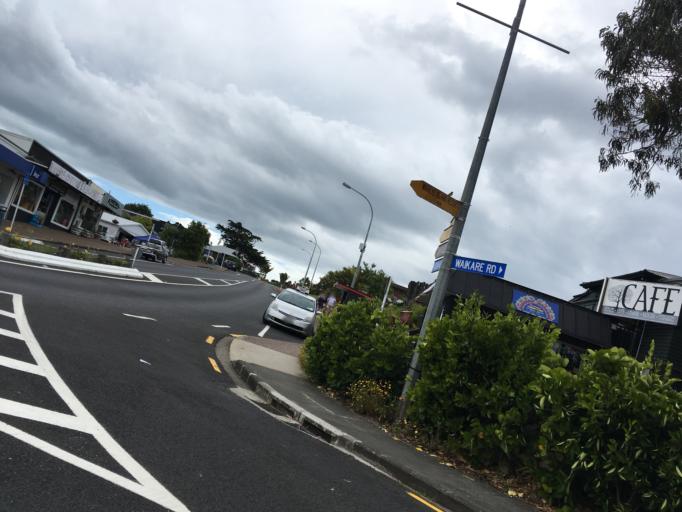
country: NZ
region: Auckland
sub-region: Auckland
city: Pakuranga
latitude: -36.7816
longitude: 175.0088
